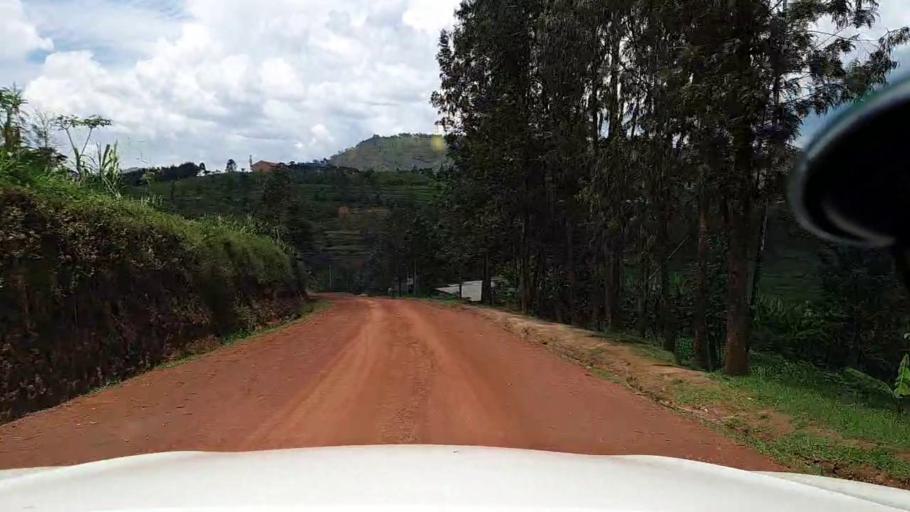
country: RW
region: Northern Province
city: Musanze
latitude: -1.6903
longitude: 29.8231
